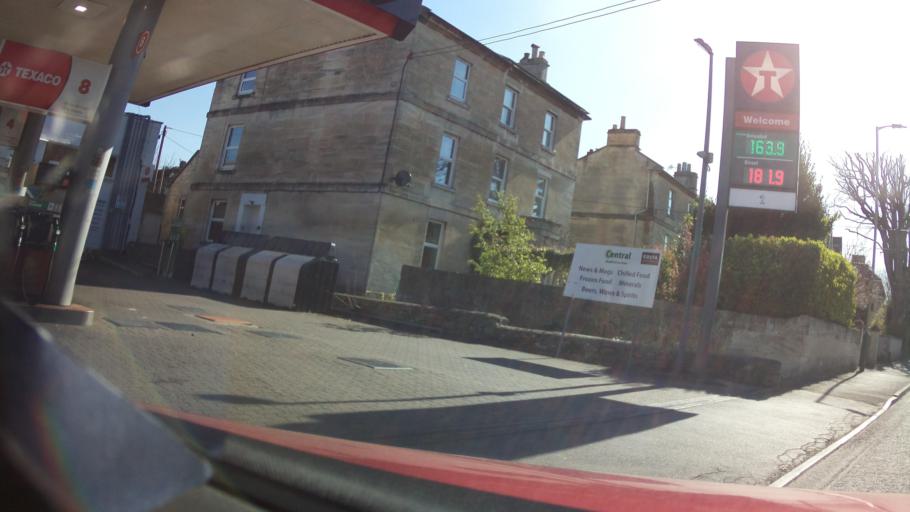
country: GB
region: England
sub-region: Wiltshire
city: Bradford-on-Avon
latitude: 51.3428
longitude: -2.2481
